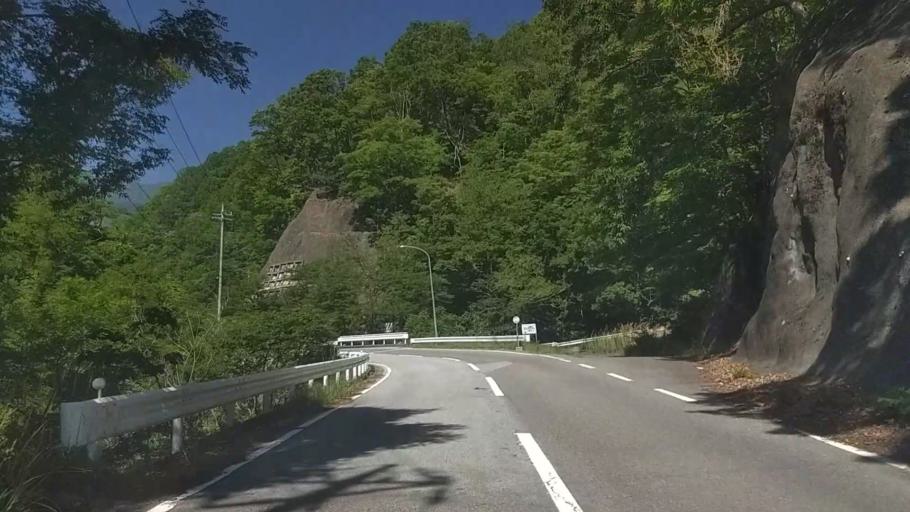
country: JP
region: Yamanashi
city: Ryuo
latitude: 35.5122
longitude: 138.4448
